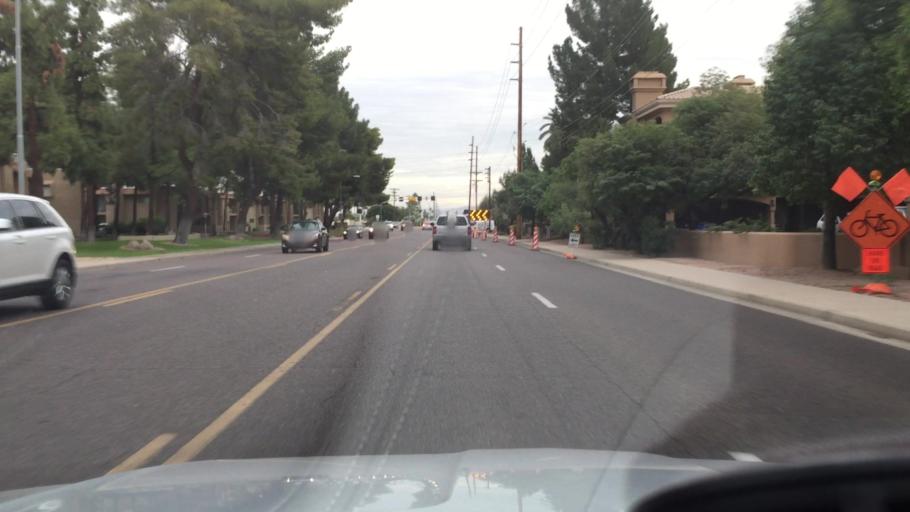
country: US
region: Arizona
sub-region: Maricopa County
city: Scottsdale
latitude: 33.5096
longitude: -111.9218
